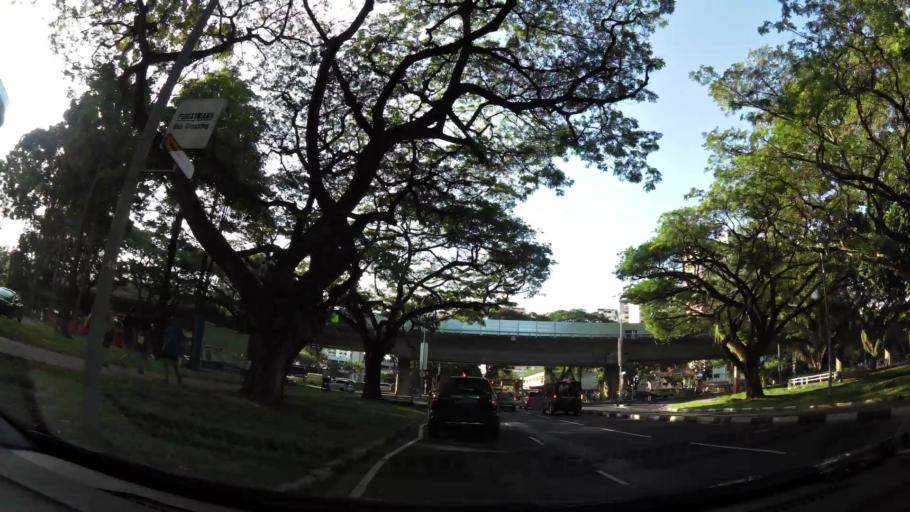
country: SG
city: Singapore
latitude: 1.3259
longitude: 103.9404
